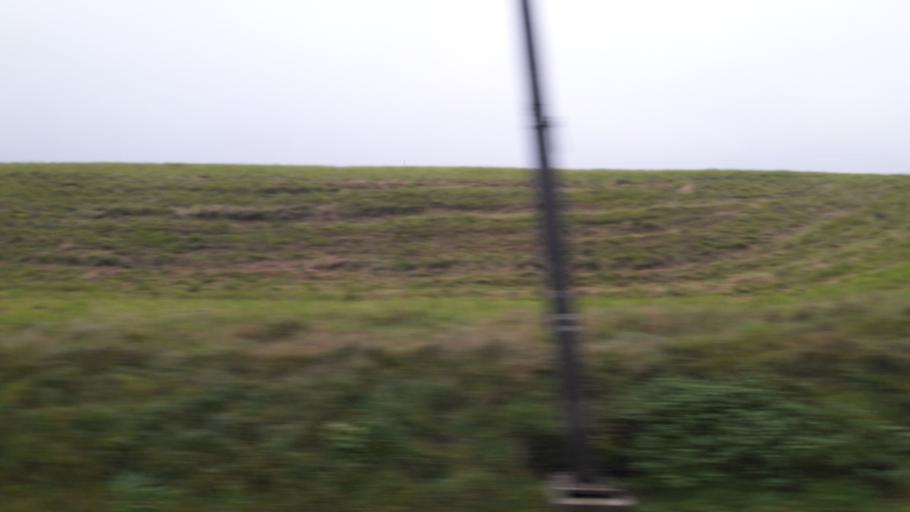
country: CH
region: Bern
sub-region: Oberaargau
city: Oberbipp
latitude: 47.2508
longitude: 7.6807
